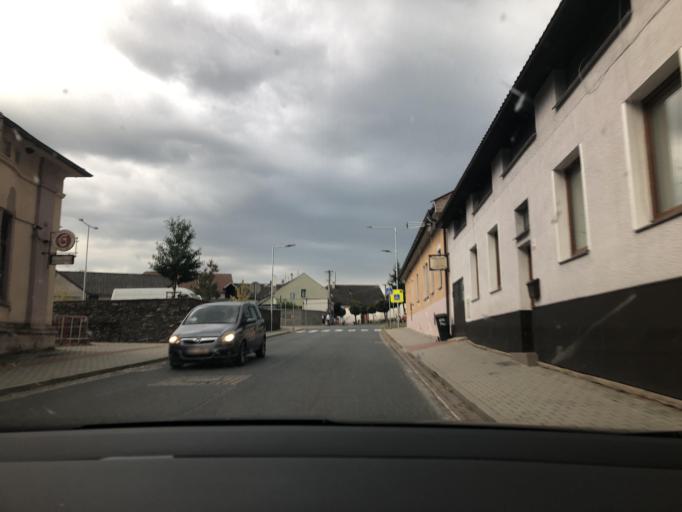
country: CZ
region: Central Bohemia
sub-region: Okres Kolin
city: Tynec nad Labem
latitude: 50.0445
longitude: 15.3596
